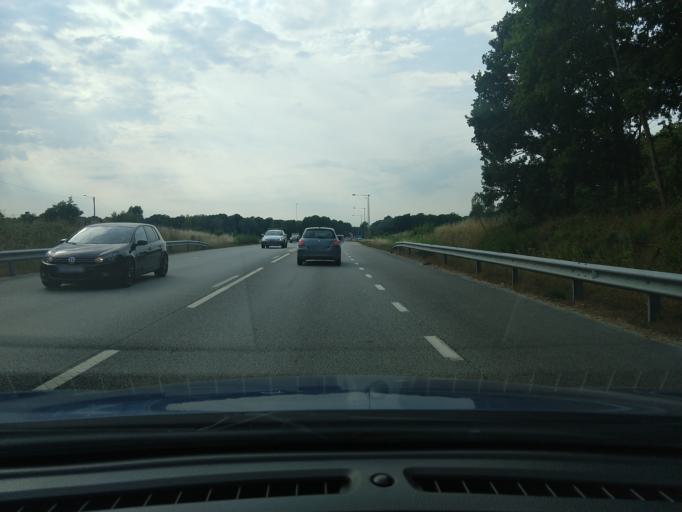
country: SE
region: Blekinge
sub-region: Karlskrona Kommun
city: Rodeby
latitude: 56.1977
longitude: 15.6879
